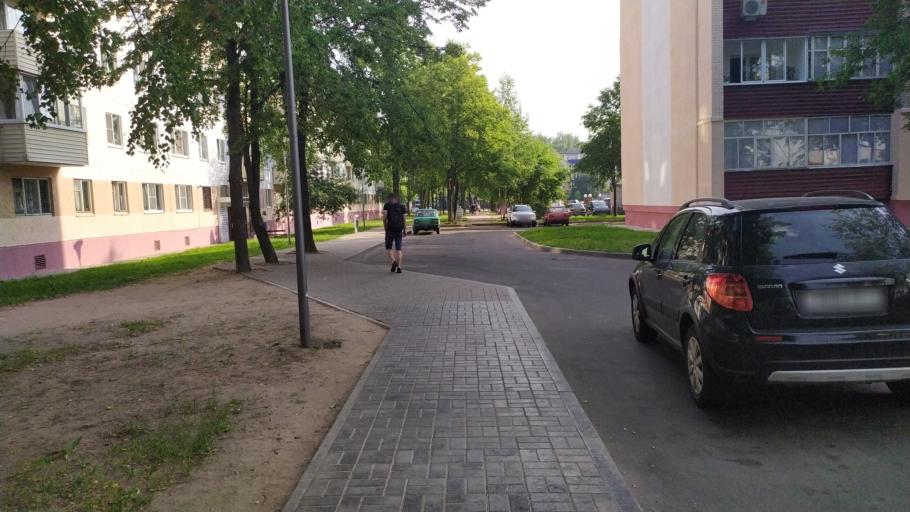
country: BY
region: Vitebsk
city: Navapolatsk
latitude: 55.5325
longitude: 28.6515
